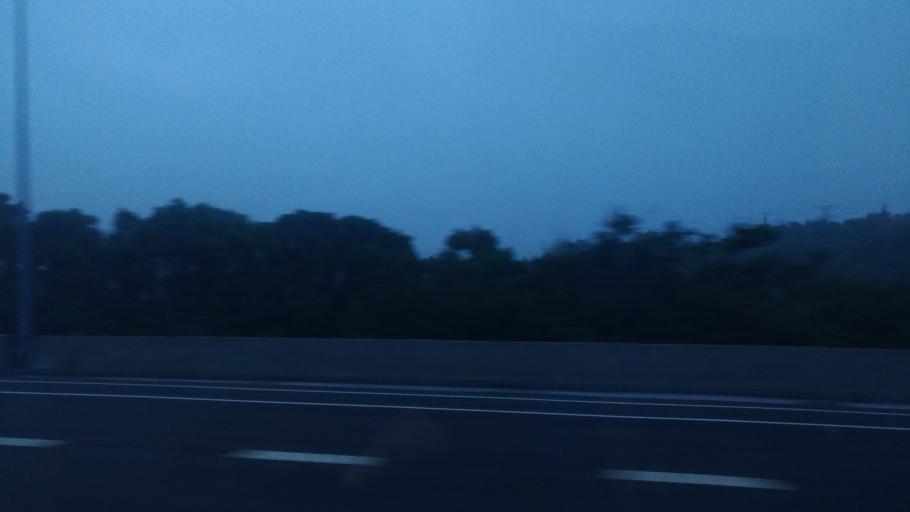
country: TW
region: Taiwan
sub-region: Miaoli
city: Miaoli
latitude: 24.5853
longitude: 120.7280
